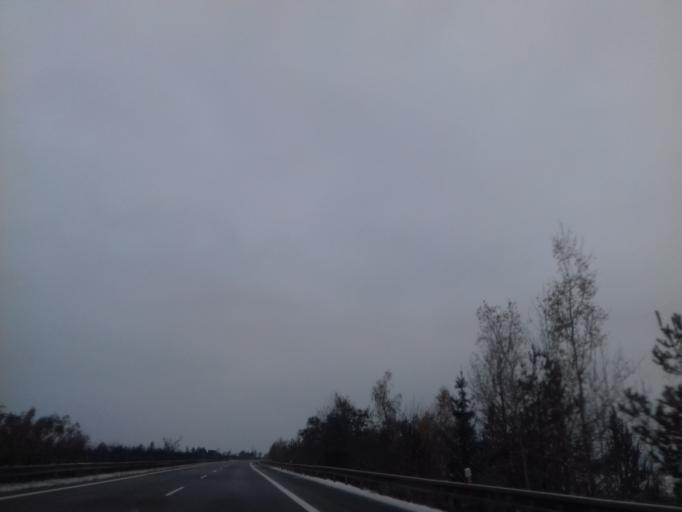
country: CZ
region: Plzensky
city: Zbiroh
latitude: 49.8293
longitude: 13.7790
